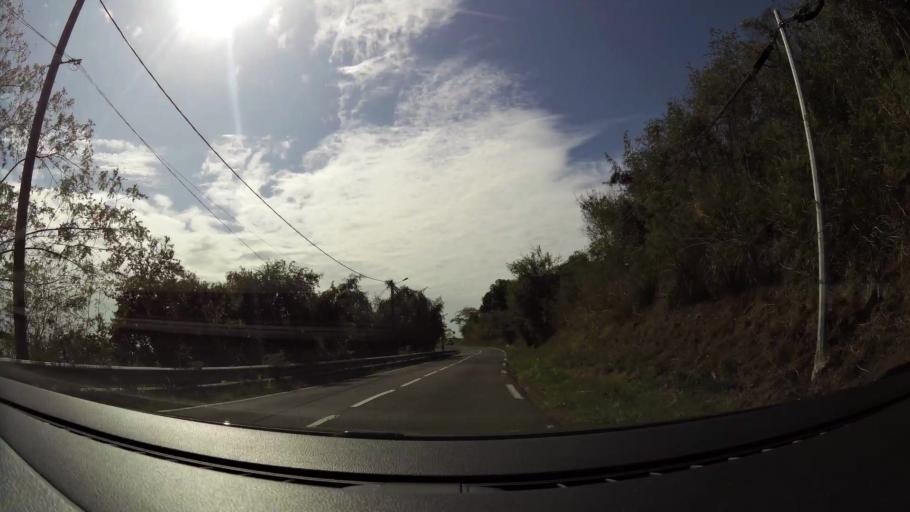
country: GP
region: Guadeloupe
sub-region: Guadeloupe
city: Vieux-Habitants
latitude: 16.0433
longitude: -61.7541
